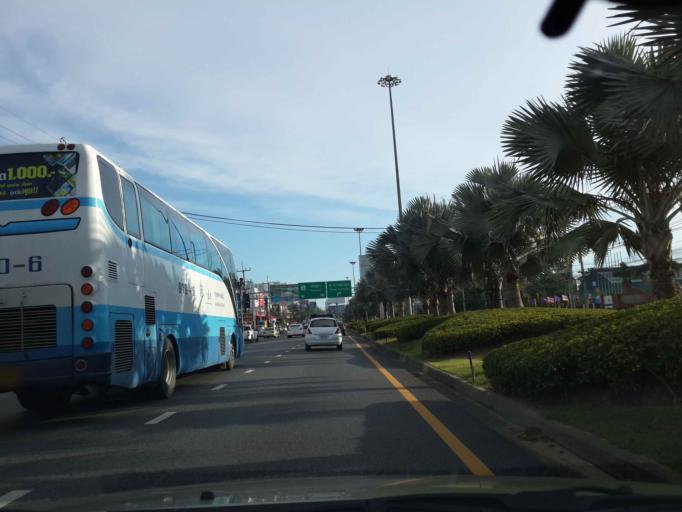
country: TH
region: Chon Buri
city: Phatthaya
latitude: 12.9774
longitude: 100.9159
